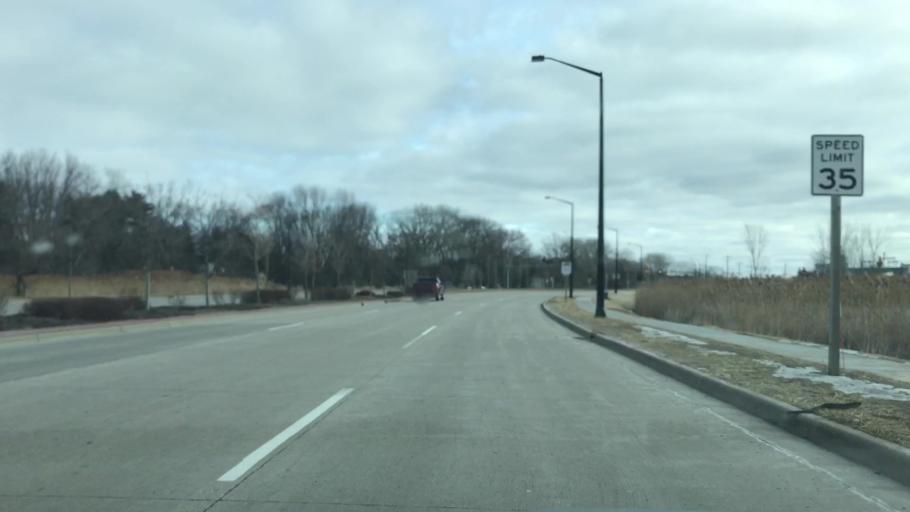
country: US
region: Wisconsin
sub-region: Brown County
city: Ashwaubenon
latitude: 44.5089
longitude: -88.0799
